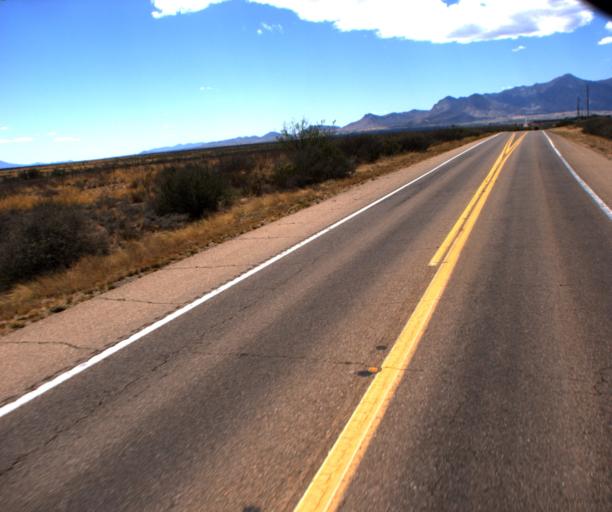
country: US
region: Arizona
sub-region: Cochise County
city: Naco
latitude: 31.3800
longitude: -110.0553
